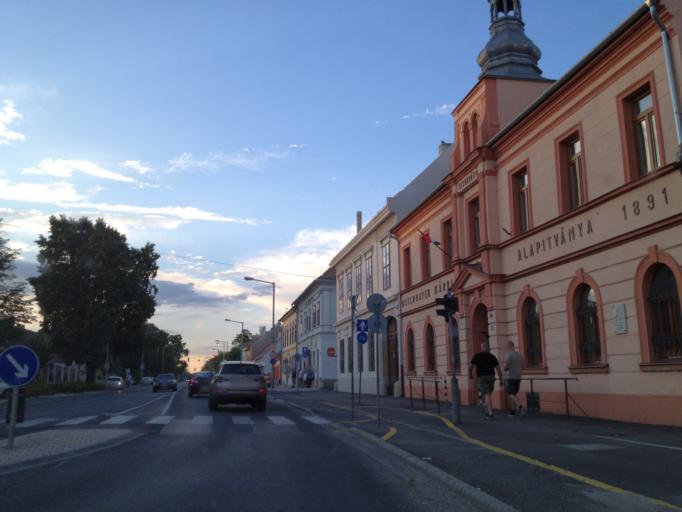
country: HU
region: Gyor-Moson-Sopron
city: Mosonmagyarovar
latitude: 47.8584
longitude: 17.2762
